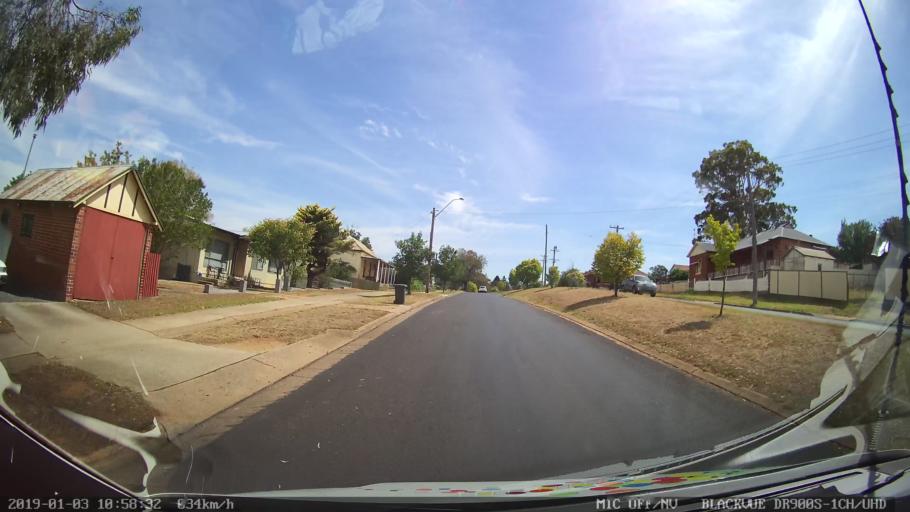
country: AU
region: New South Wales
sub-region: Young
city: Young
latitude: -34.3104
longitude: 148.2962
